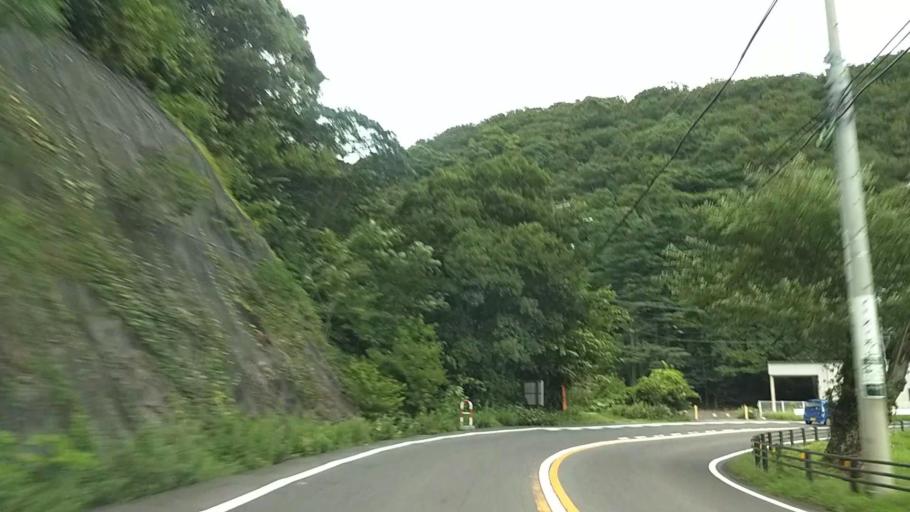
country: JP
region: Shizuoka
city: Ito
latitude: 35.0268
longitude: 139.0958
